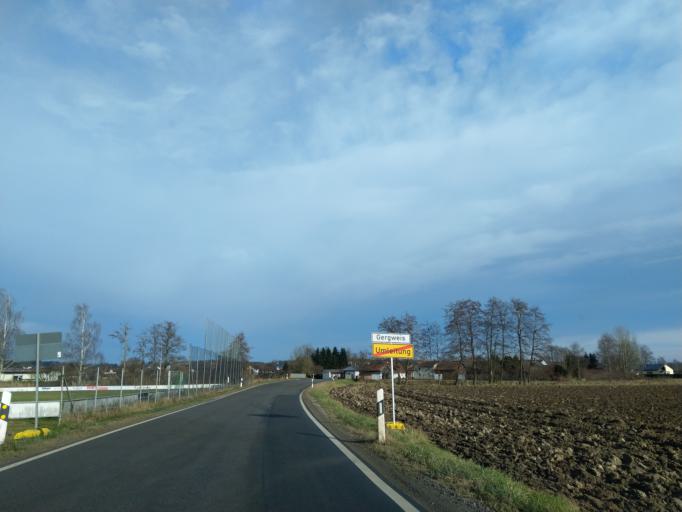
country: DE
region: Bavaria
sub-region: Lower Bavaria
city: Rossbach
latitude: 48.6206
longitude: 12.9558
